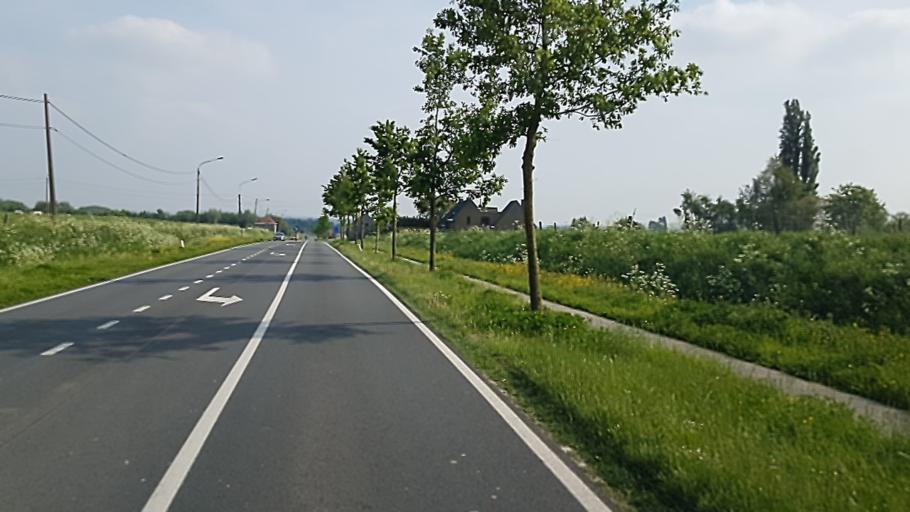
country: BE
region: Flanders
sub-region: Provincie West-Vlaanderen
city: Zwevegem
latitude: 50.7575
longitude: 3.3117
